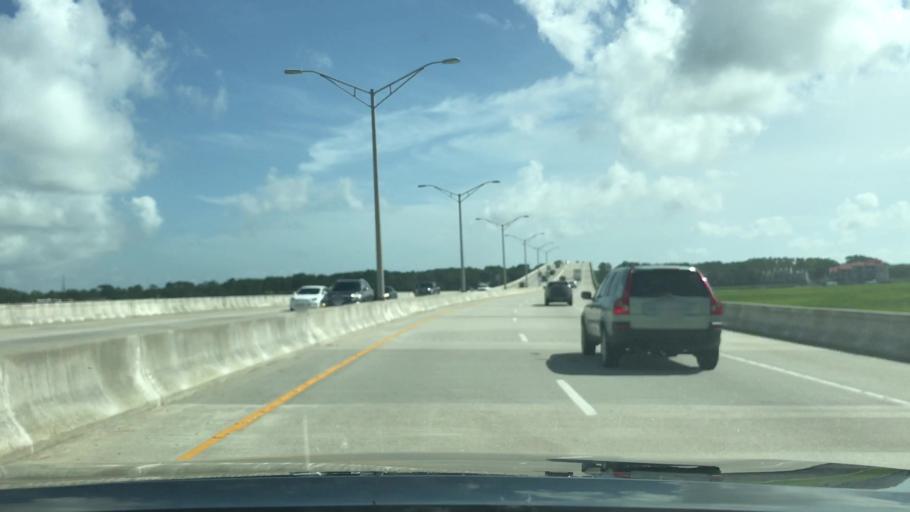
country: US
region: South Carolina
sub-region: Beaufort County
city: Hilton Head Island
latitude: 32.1835
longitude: -80.7659
